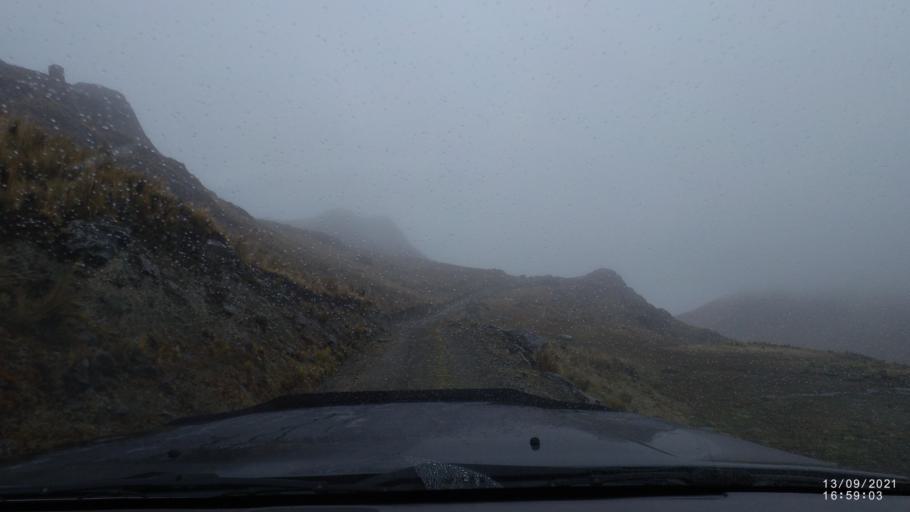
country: BO
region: Cochabamba
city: Colomi
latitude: -17.3096
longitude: -65.7146
